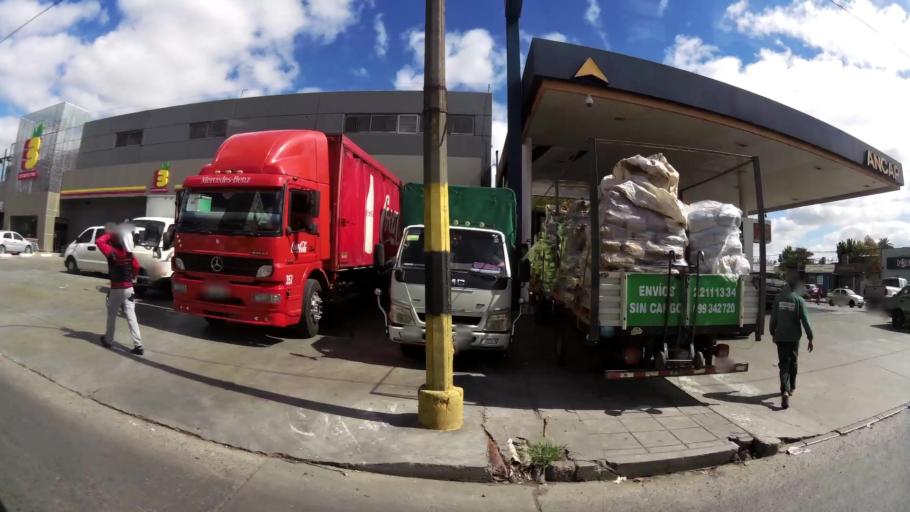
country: UY
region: Canelones
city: Paso de Carrasco
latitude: -34.8713
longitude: -56.1163
